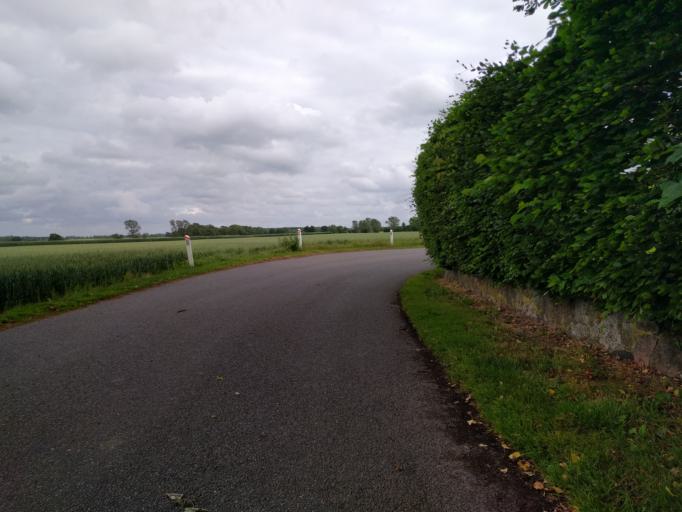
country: DK
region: South Denmark
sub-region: Kerteminde Kommune
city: Munkebo
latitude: 55.4110
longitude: 10.5439
